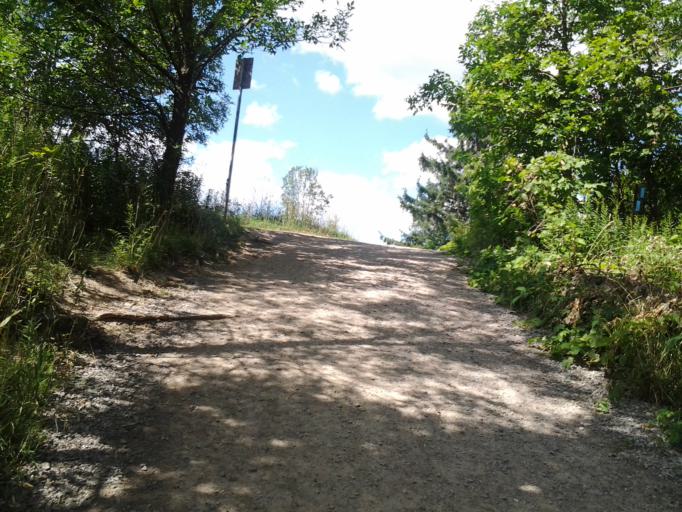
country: CA
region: Ontario
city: Ancaster
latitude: 43.2809
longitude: -79.9790
